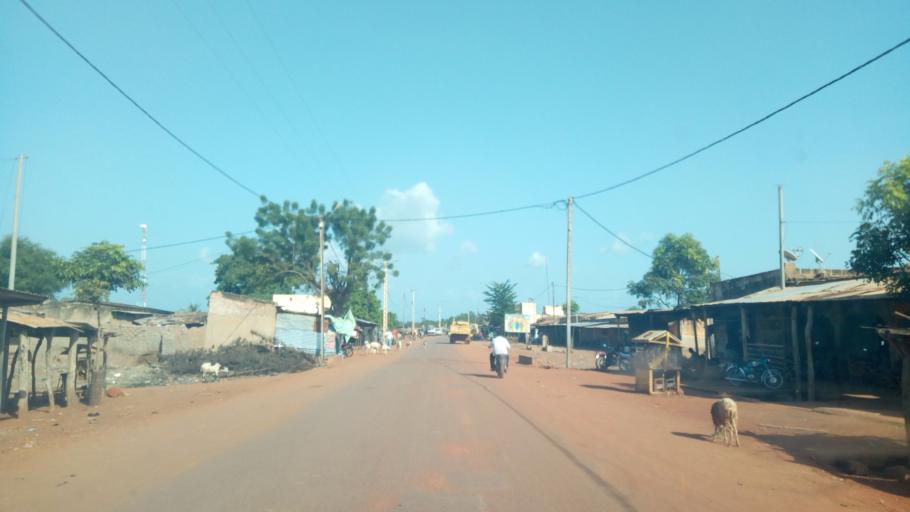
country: ML
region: Sikasso
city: Yorosso
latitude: 12.1831
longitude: -4.8050
